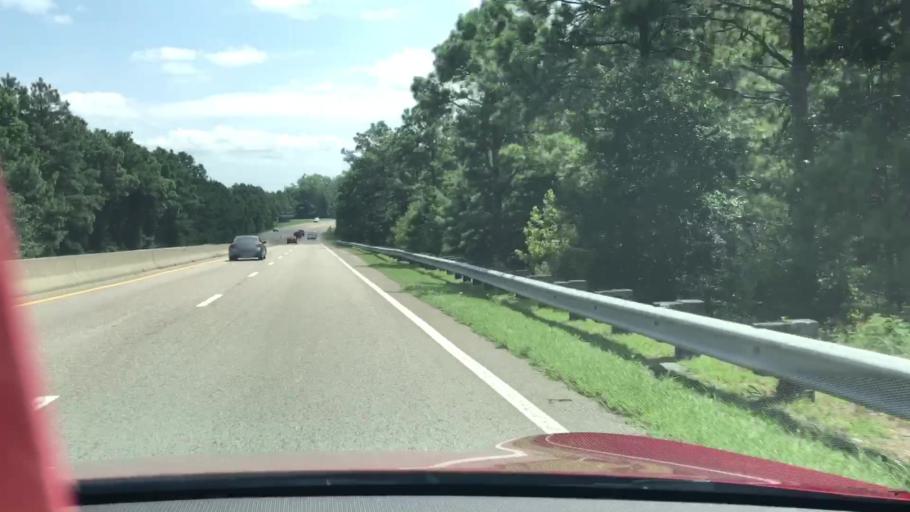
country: US
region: North Carolina
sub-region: Currituck County
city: Currituck
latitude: 36.3383
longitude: -75.9516
